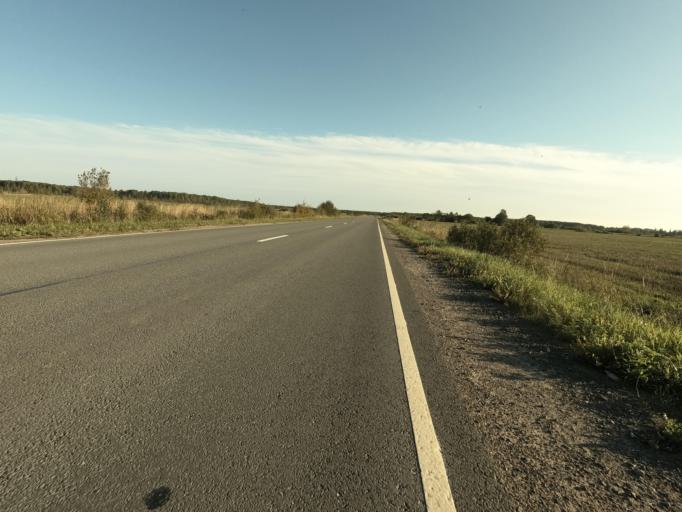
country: RU
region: St.-Petersburg
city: Sapernyy
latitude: 59.7404
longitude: 30.6511
